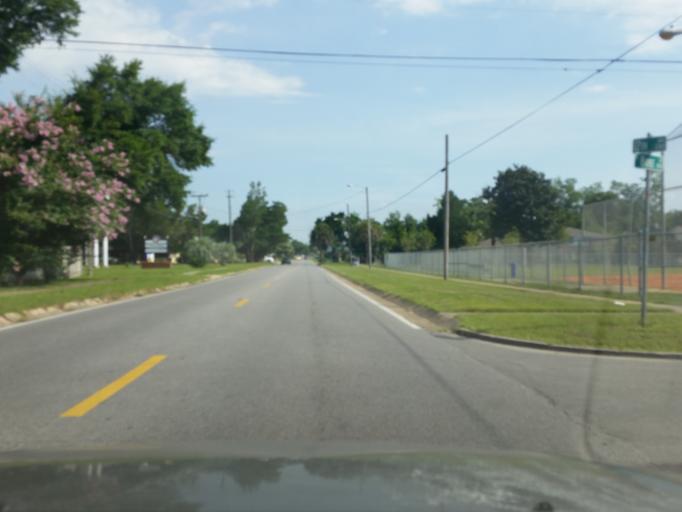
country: US
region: Florida
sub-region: Escambia County
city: Goulding
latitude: 30.4381
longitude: -87.2058
